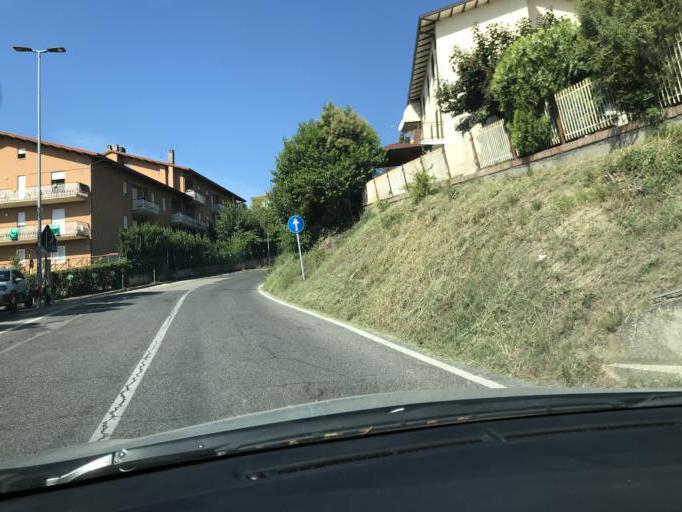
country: IT
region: Umbria
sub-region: Provincia di Perugia
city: Ponte Felcino
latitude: 43.1055
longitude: 12.4340
